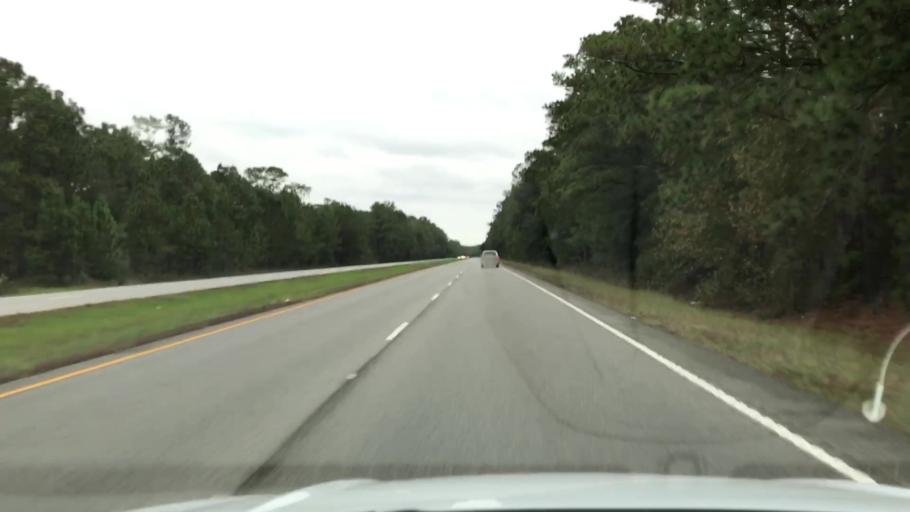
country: US
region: South Carolina
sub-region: Georgetown County
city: Georgetown
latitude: 33.3925
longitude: -79.2030
